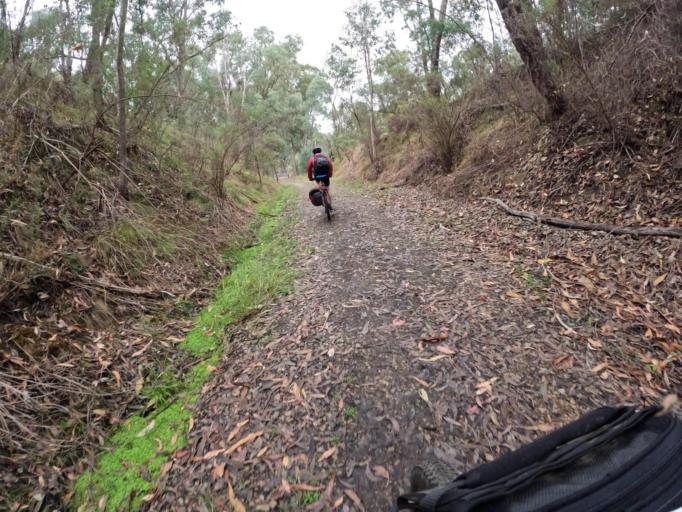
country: AU
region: New South Wales
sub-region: Greater Hume Shire
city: Holbrook
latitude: -36.1675
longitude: 147.4056
